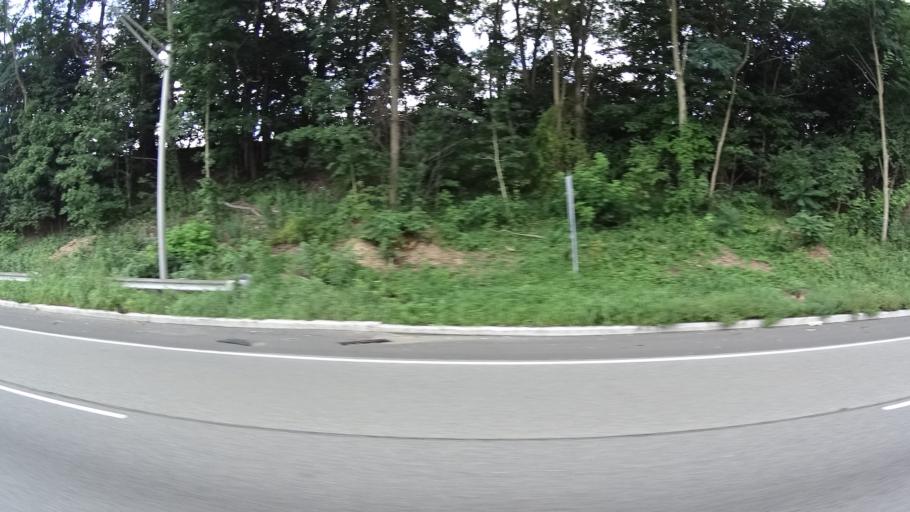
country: US
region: New Jersey
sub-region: Union County
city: Springfield
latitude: 40.7184
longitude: -74.3322
